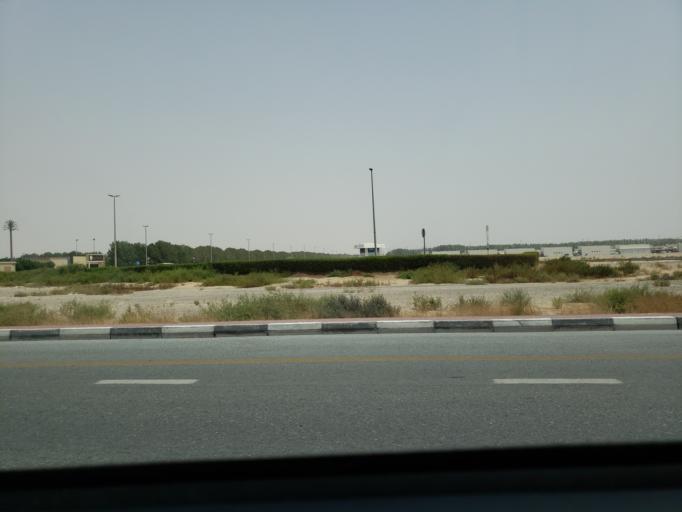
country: AE
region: Ash Shariqah
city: Sharjah
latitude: 25.3540
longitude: 55.4796
